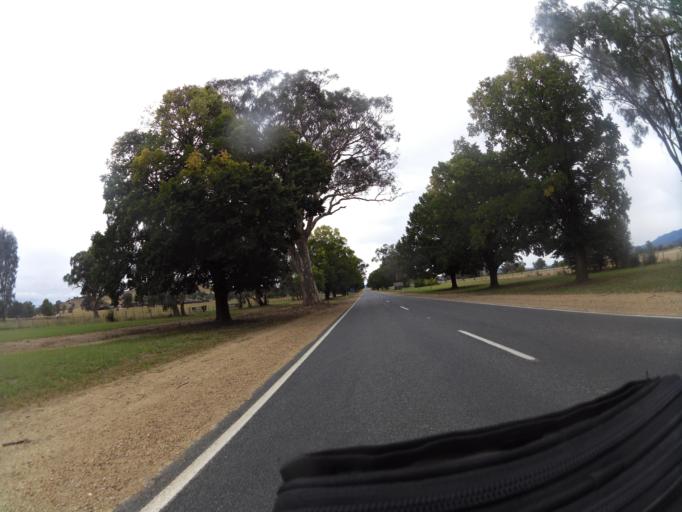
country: AU
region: New South Wales
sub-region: Snowy River
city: Jindabyne
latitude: -36.1830
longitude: 147.9224
